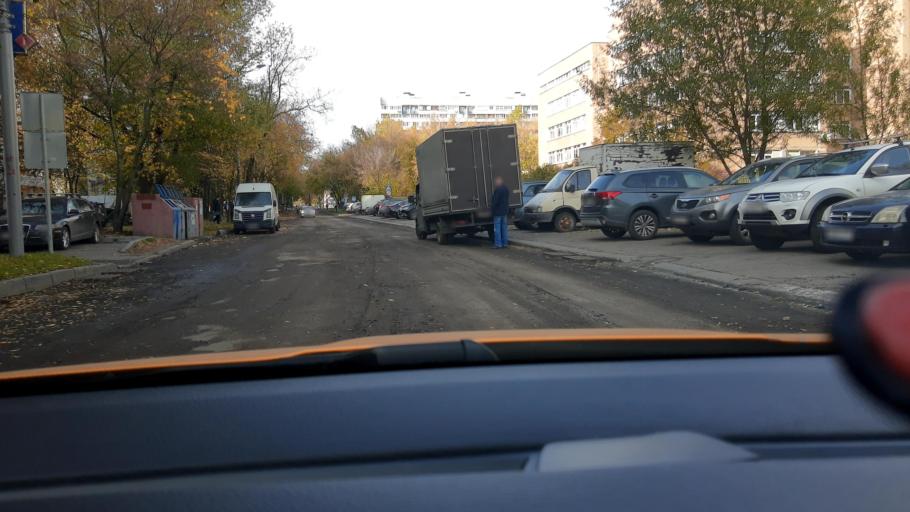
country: RU
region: Moscow
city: Babushkin
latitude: 55.8764
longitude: 37.7267
